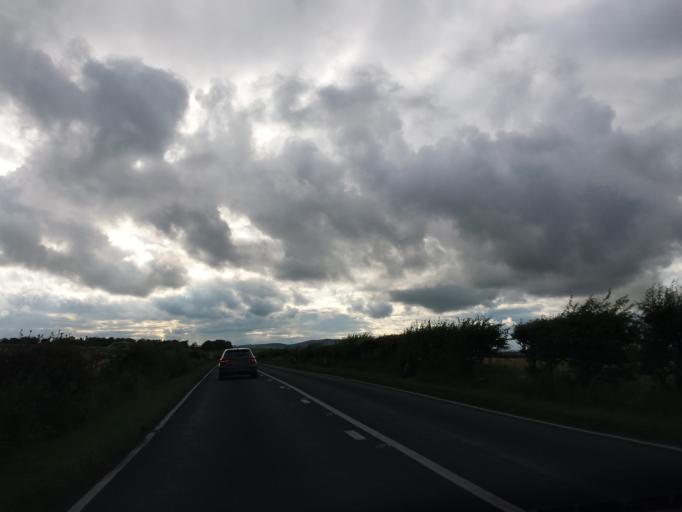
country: GB
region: Scotland
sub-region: Fife
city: Strathkinness
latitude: 56.3513
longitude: -2.8420
